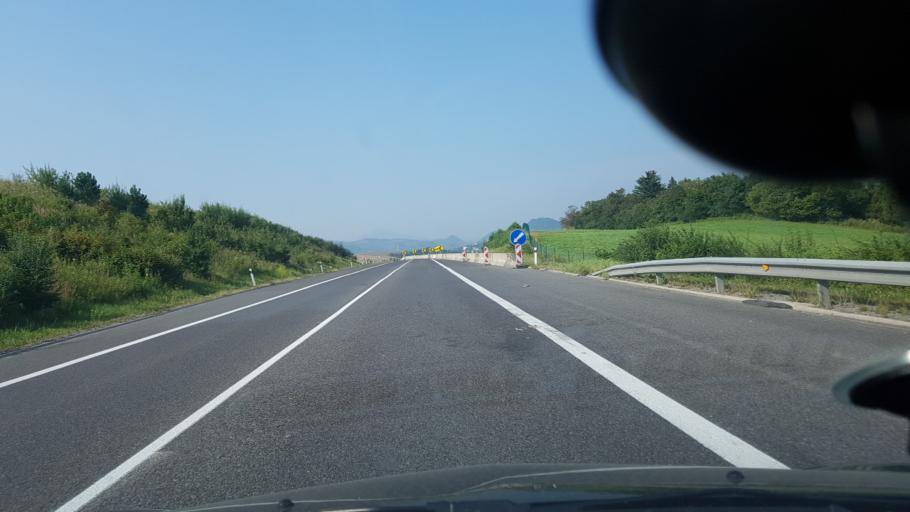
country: SK
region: Zilinsky
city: Tvrdosin
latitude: 49.3470
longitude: 19.5812
